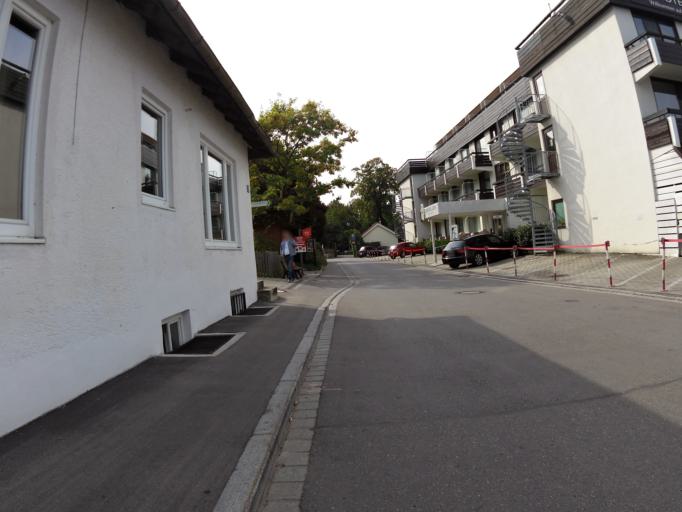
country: DE
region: Bavaria
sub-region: Upper Bavaria
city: Berg
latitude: 47.9557
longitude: 11.3440
